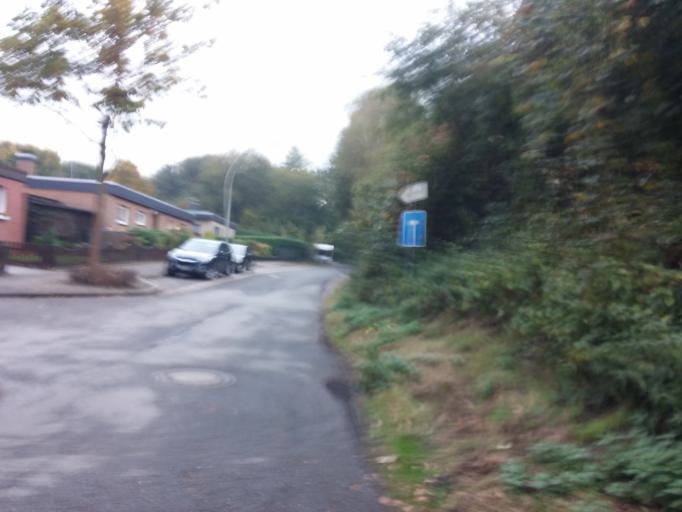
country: DE
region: North Rhine-Westphalia
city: Dorsten
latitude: 51.6528
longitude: 6.9477
